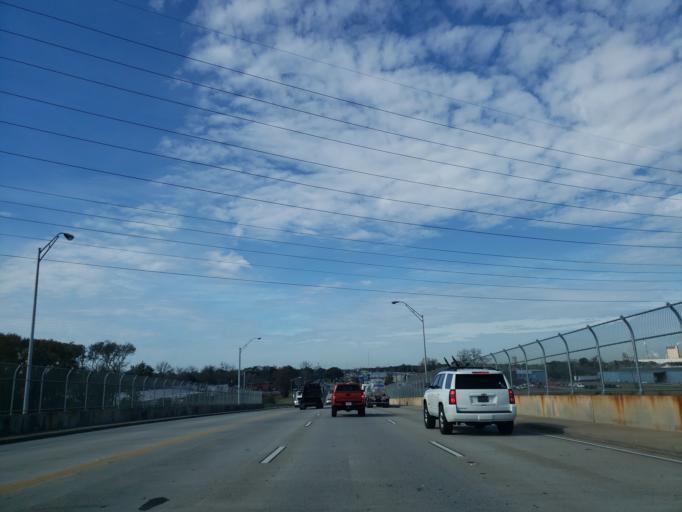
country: US
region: Georgia
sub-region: Chatham County
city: Savannah
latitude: 32.0854
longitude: -81.1080
